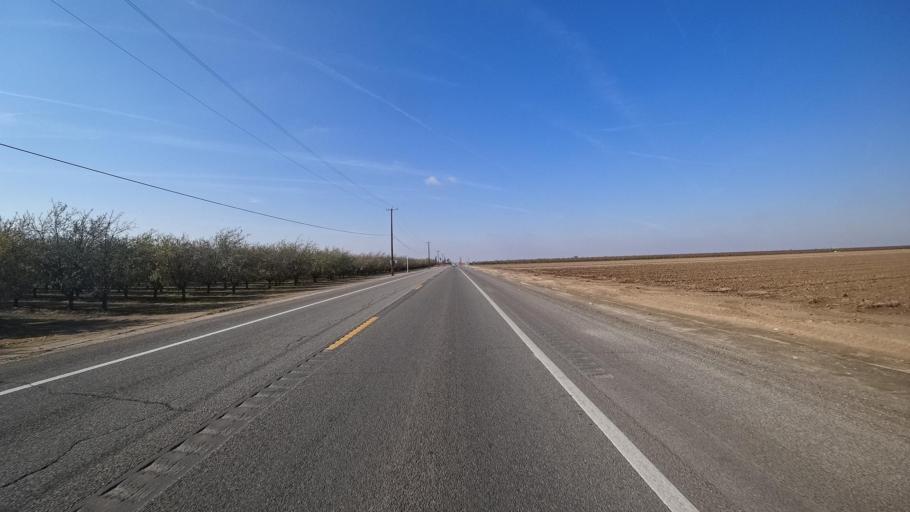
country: US
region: California
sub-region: Kern County
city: Arvin
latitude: 35.2089
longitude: -118.8612
